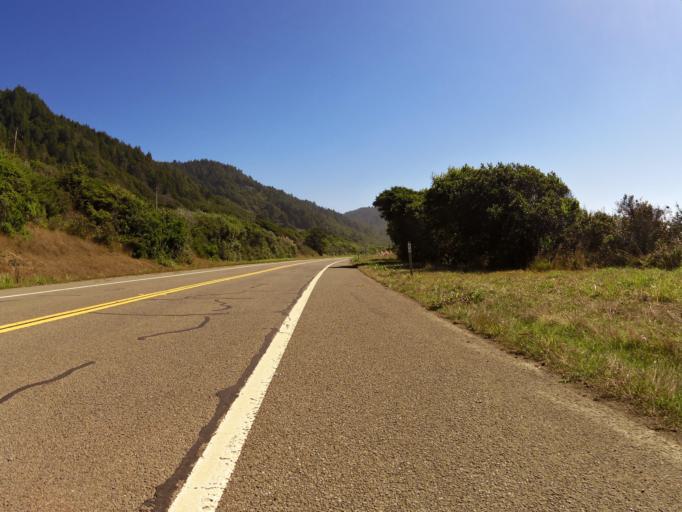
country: US
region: California
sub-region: Mendocino County
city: Fort Bragg
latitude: 39.6913
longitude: -123.7946
